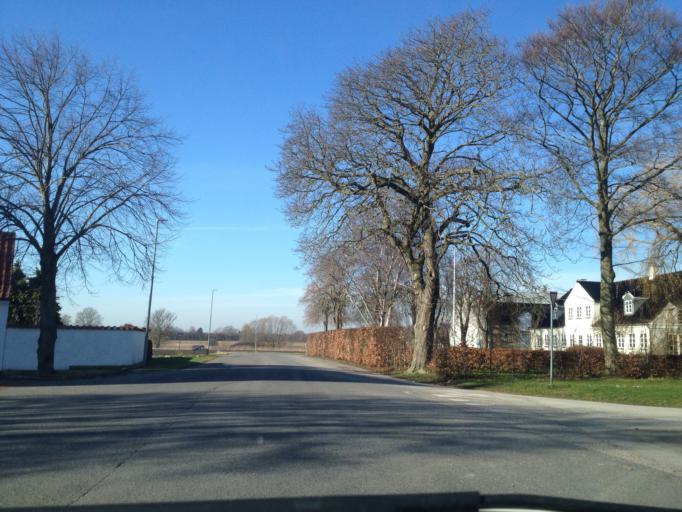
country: DK
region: South Denmark
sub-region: Nyborg Kommune
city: Ullerslev
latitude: 55.3824
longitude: 10.7225
